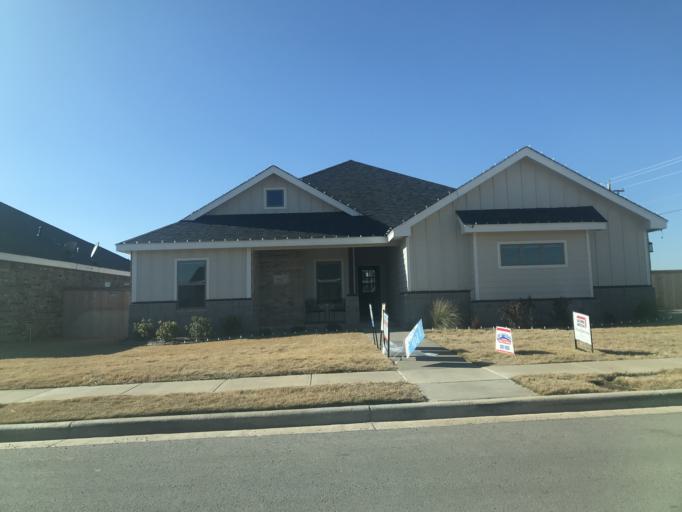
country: US
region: Texas
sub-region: Taylor County
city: Potosi
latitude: 32.3719
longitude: -99.7205
